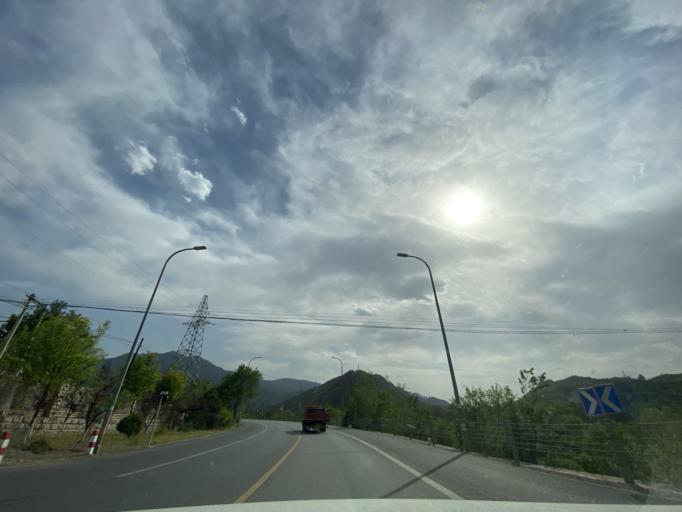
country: CN
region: Beijing
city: Miaofengshan
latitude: 39.9869
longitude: 116.0619
